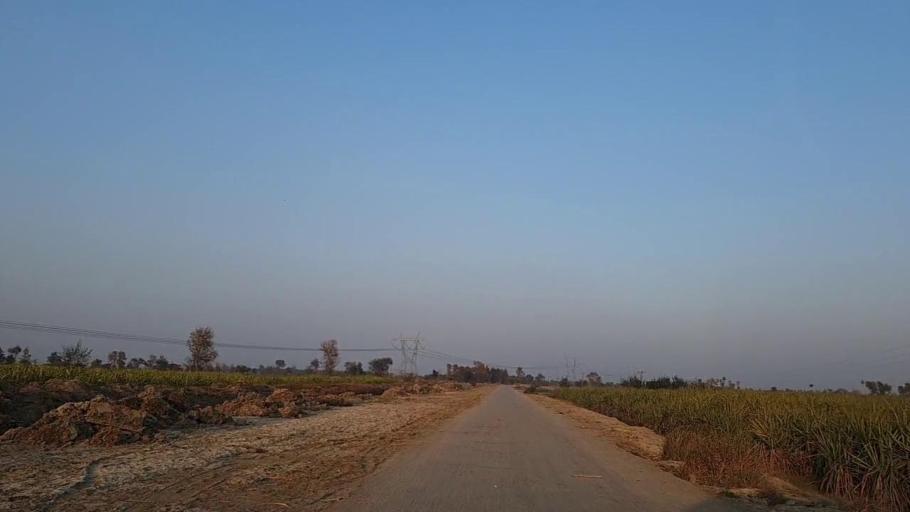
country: PK
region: Sindh
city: Moro
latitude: 26.7642
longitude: 68.0437
